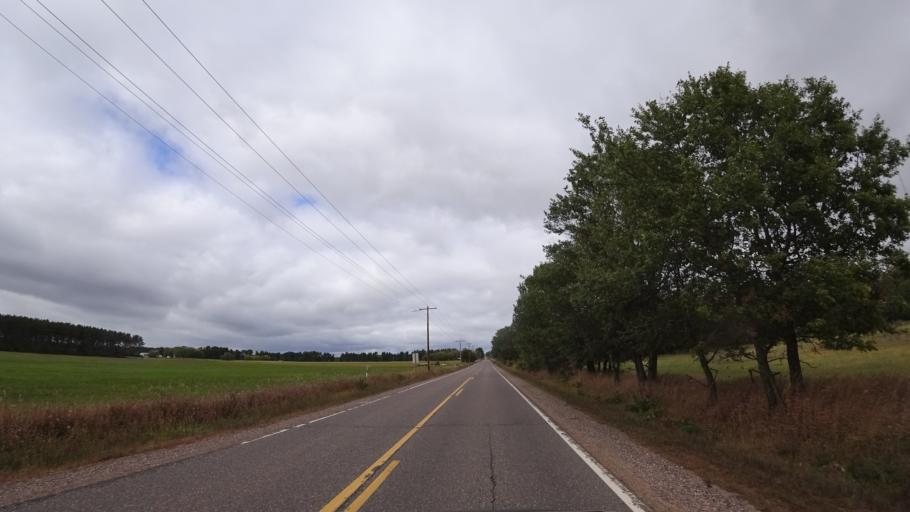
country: US
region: Wisconsin
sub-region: Chippewa County
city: Lake Wissota
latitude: 44.9745
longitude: -91.2678
